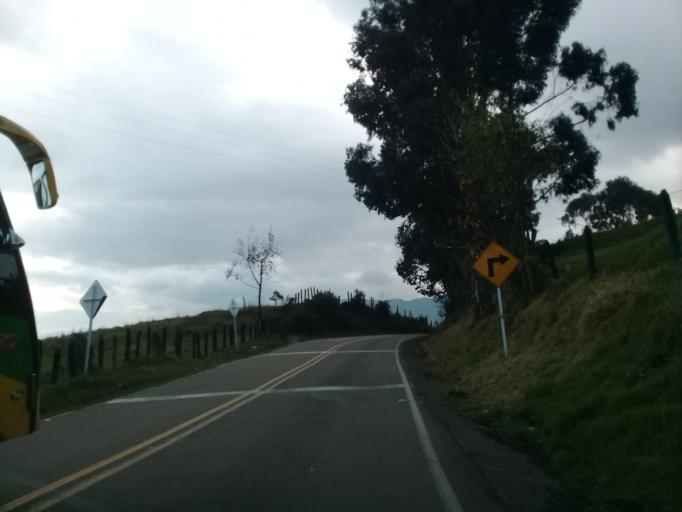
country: CO
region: Cundinamarca
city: Zipaquira
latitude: 5.0370
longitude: -74.0436
